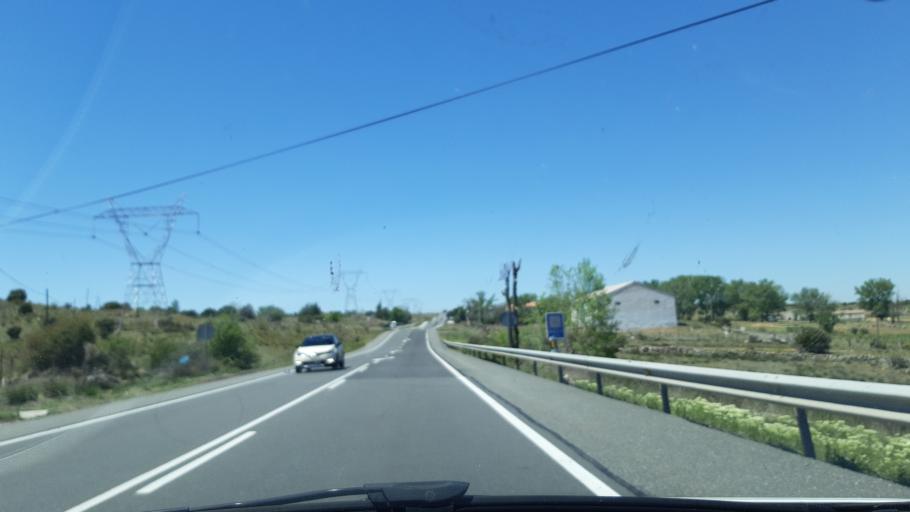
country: ES
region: Castille and Leon
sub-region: Provincia de Segovia
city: Ituero y Lama
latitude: 40.7739
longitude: -4.3834
